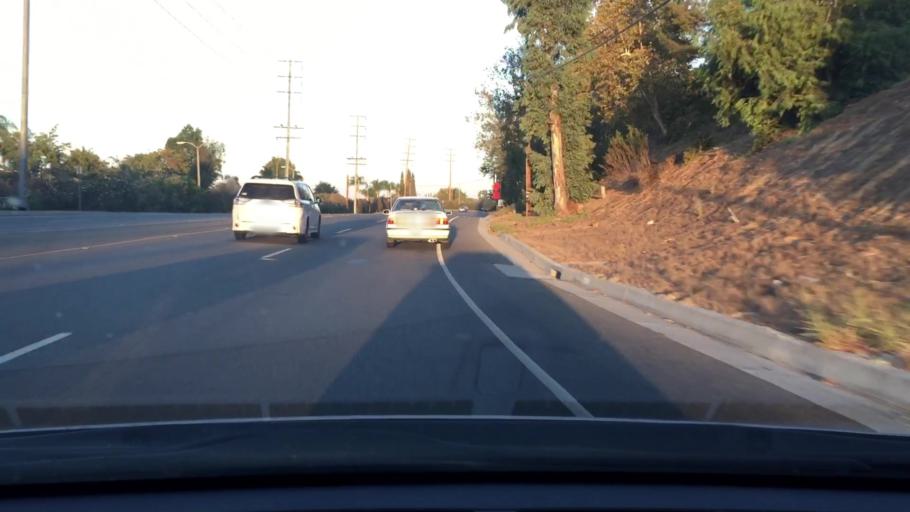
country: US
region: California
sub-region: San Bernardino County
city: Los Serranos
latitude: 33.9831
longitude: -117.7265
